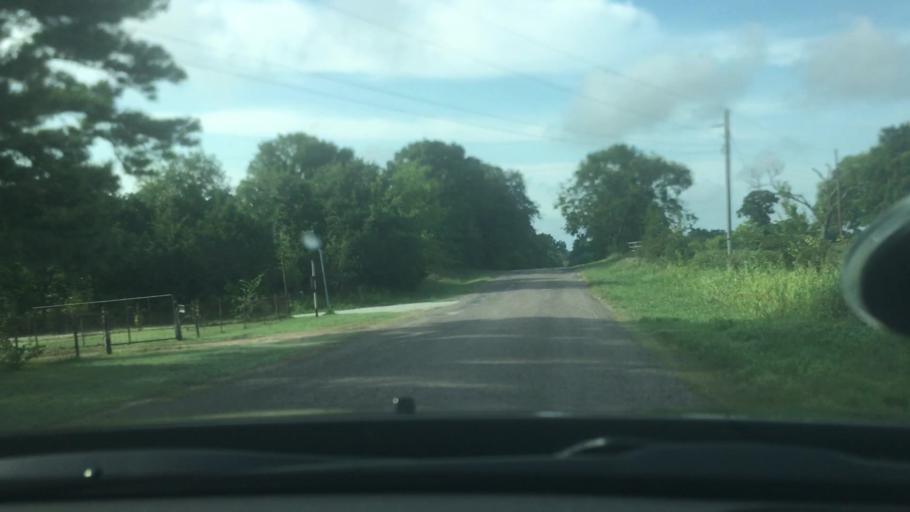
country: US
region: Oklahoma
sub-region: Pontotoc County
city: Ada
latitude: 34.6659
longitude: -96.5298
